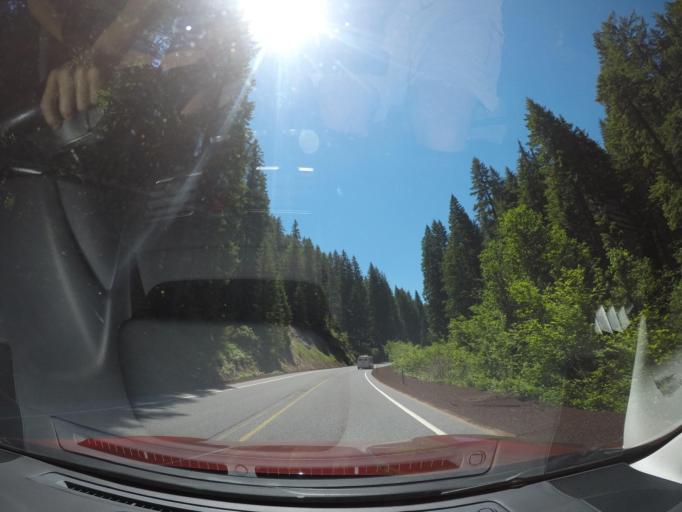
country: US
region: Oregon
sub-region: Deschutes County
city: Sisters
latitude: 44.5474
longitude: -121.9942
